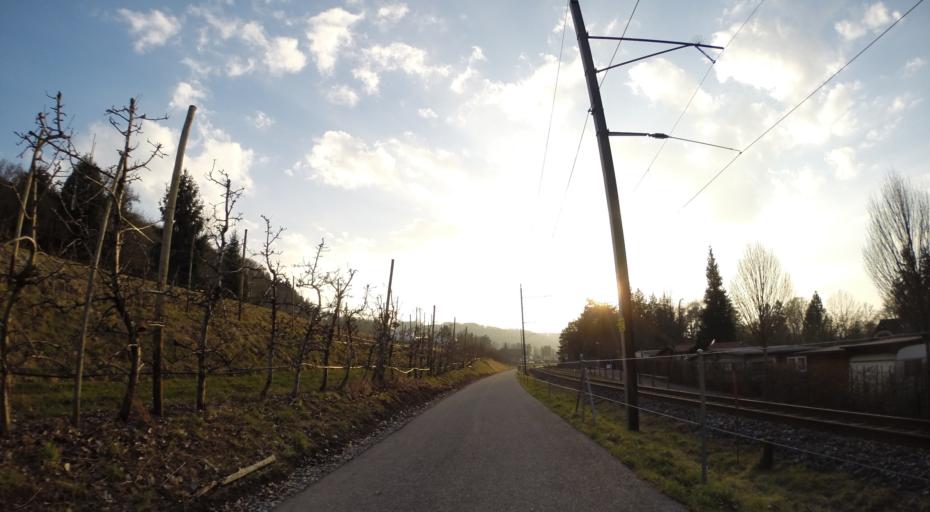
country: DE
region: Baden-Wuerttemberg
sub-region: Freiburg Region
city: Ohningen
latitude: 47.6458
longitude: 8.9246
